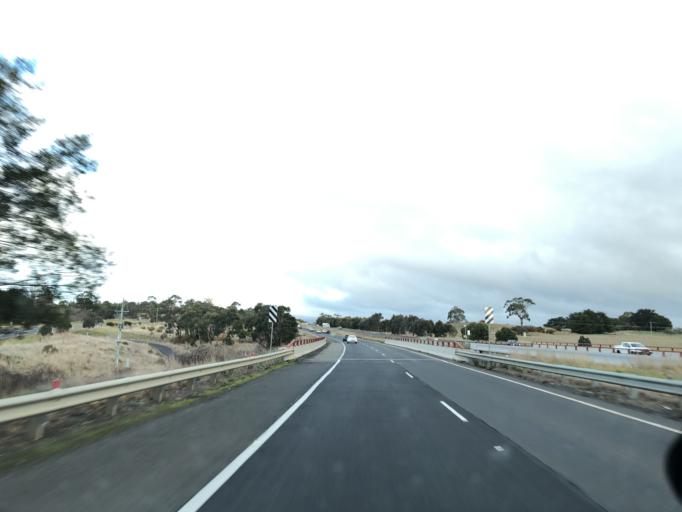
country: AU
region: Victoria
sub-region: Mount Alexander
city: Castlemaine
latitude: -37.2702
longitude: 144.4779
